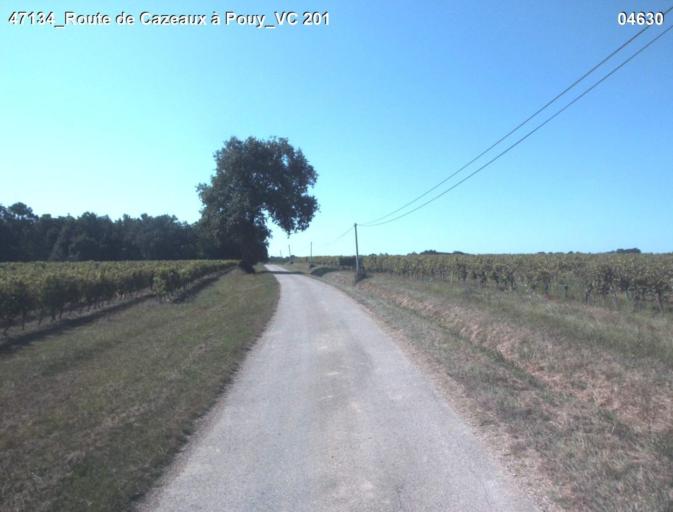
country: FR
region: Aquitaine
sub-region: Departement du Lot-et-Garonne
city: Mezin
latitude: 44.0375
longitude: 0.3126
